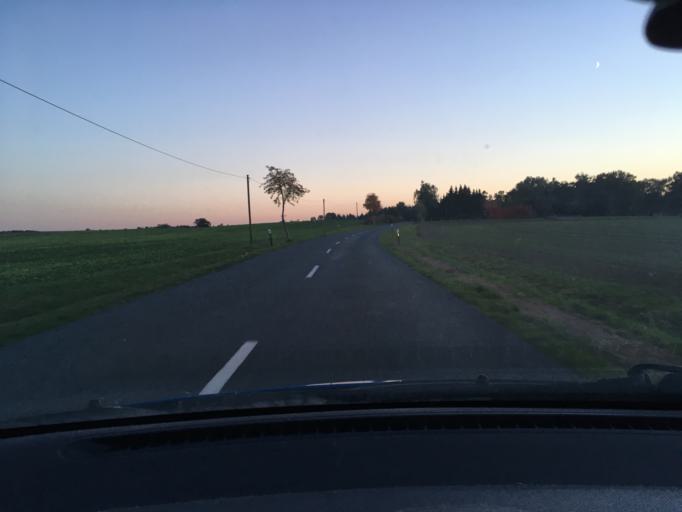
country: DE
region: Lower Saxony
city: Reinstorf
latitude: 53.2287
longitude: 10.5710
